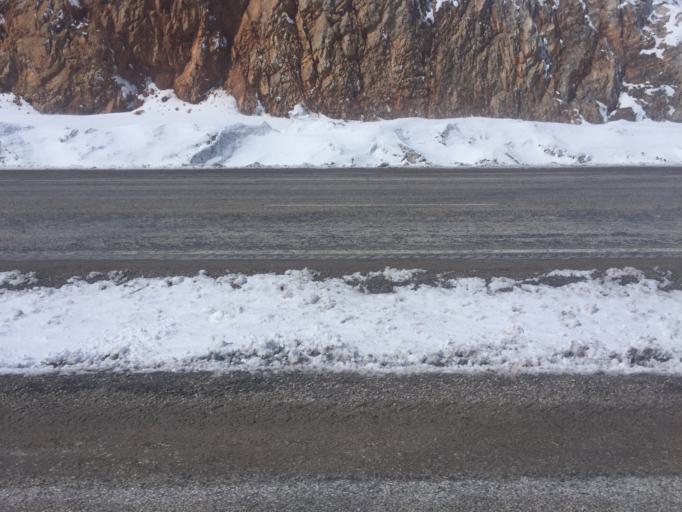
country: TR
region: Kahramanmaras
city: Goksun
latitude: 38.1900
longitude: 36.4569
